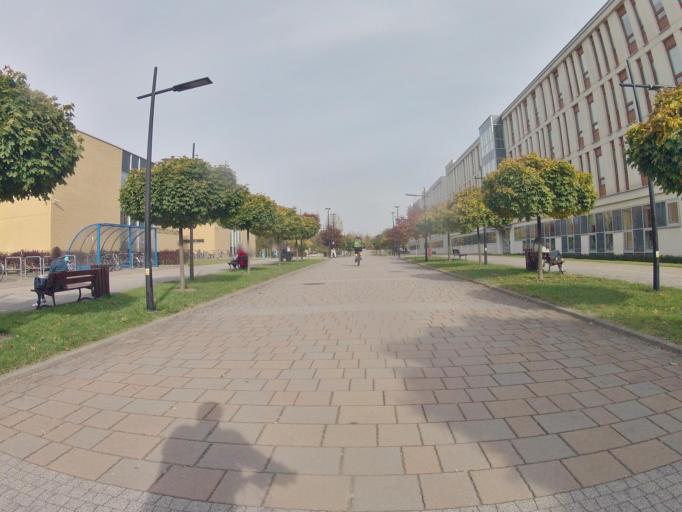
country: PL
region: Lesser Poland Voivodeship
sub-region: Krakow
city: Krakow
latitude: 50.0299
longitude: 19.9072
